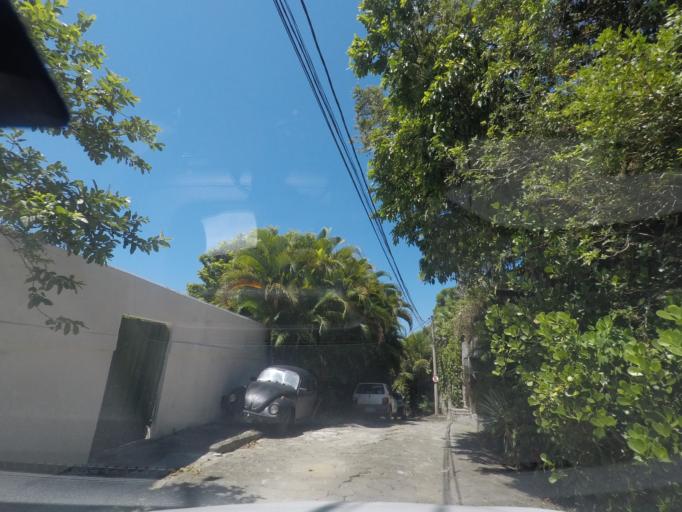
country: BR
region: Rio de Janeiro
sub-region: Niteroi
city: Niteroi
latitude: -22.9705
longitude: -43.0348
